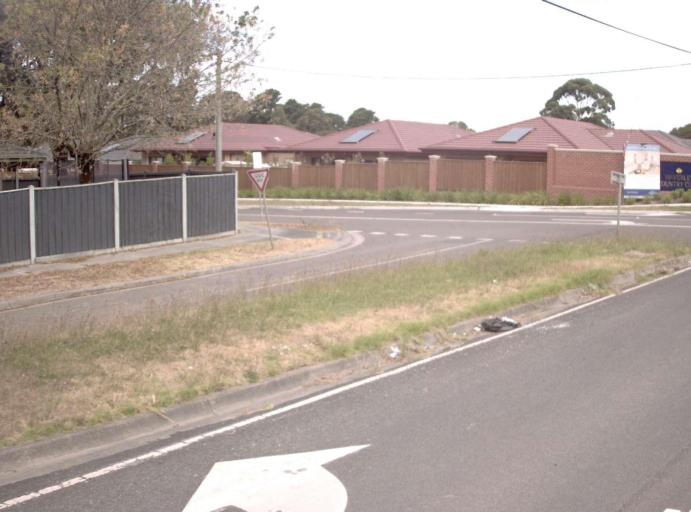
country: AU
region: Victoria
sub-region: Knox
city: Rowville
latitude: -37.9333
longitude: 145.2322
